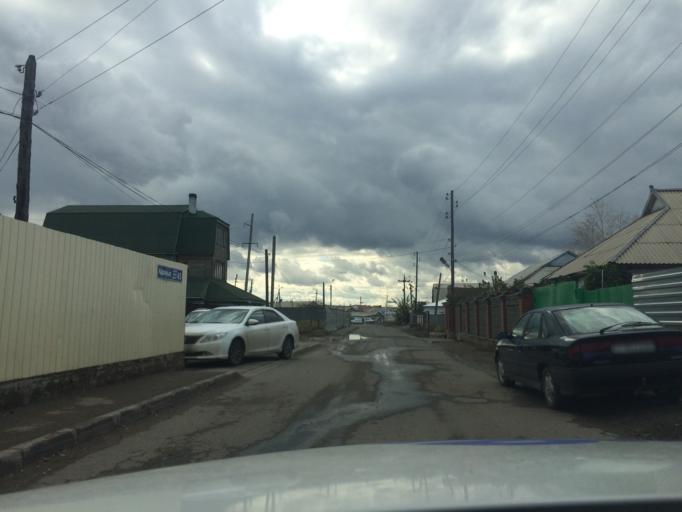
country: KZ
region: Astana Qalasy
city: Astana
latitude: 51.1846
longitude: 71.3962
